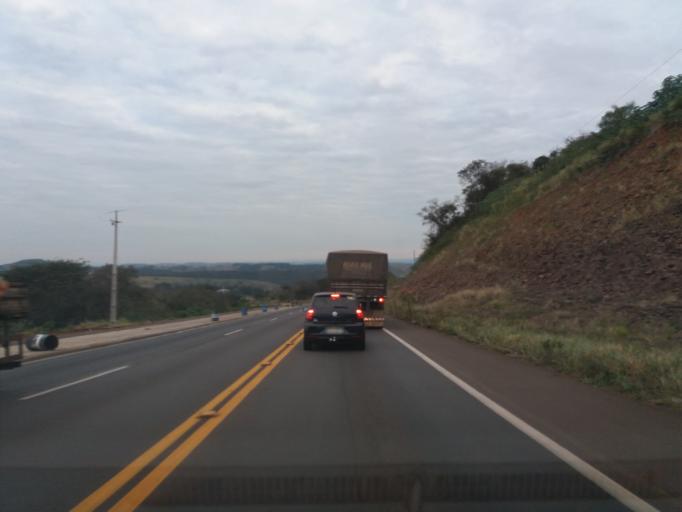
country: BR
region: Parana
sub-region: Cascavel
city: Cascavel
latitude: -25.1966
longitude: -53.6027
